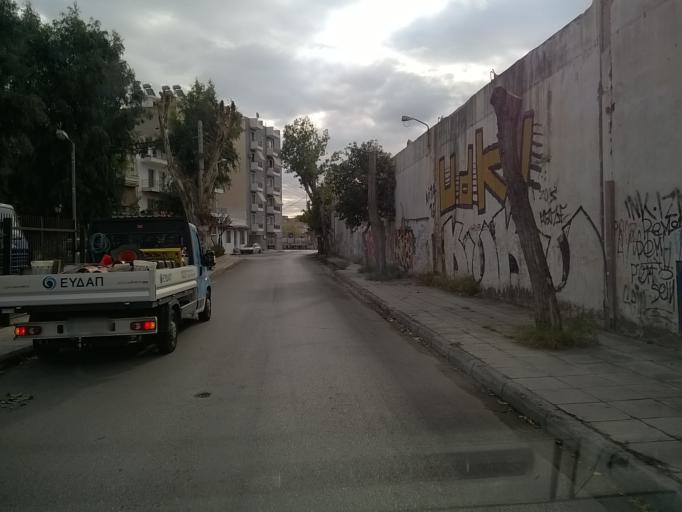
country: GR
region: Attica
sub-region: Nomarchia Athinas
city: Moskhaton
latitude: 37.9471
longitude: 23.6603
